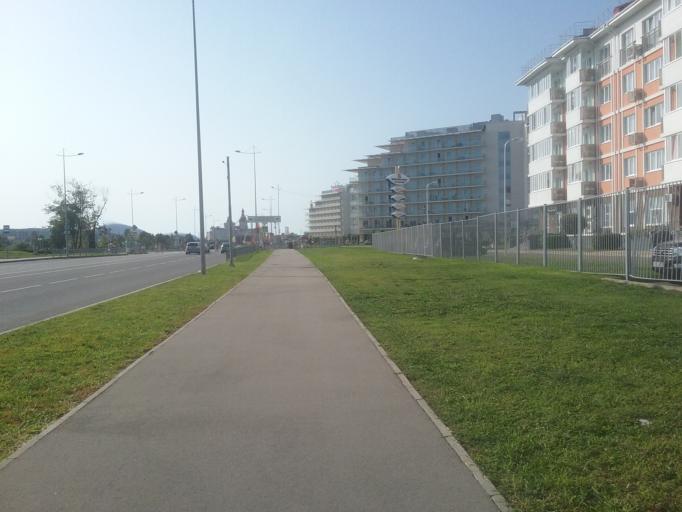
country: RU
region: Krasnodarskiy
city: Adler
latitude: 43.4003
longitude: 39.9786
